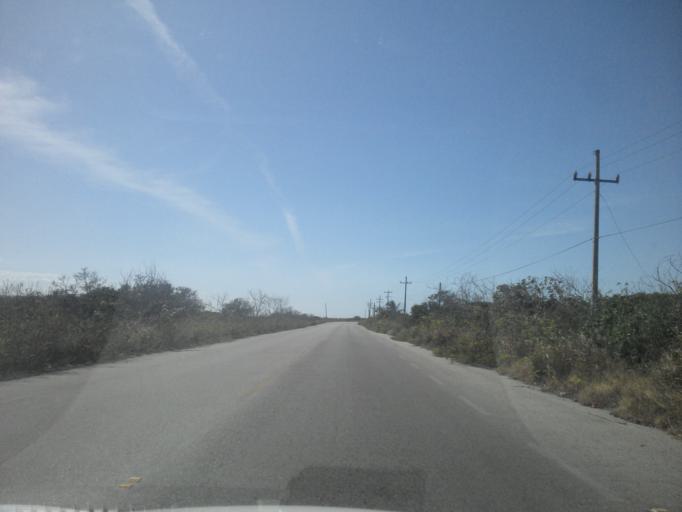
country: MX
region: Yucatan
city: Telchac Puerto
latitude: 21.3318
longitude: -89.3583
